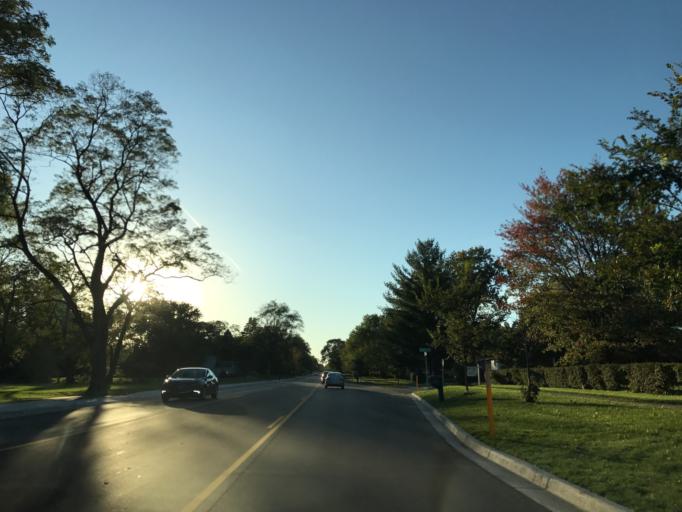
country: US
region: Michigan
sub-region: Oakland County
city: Farmington Hills
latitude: 42.4849
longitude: -83.3521
